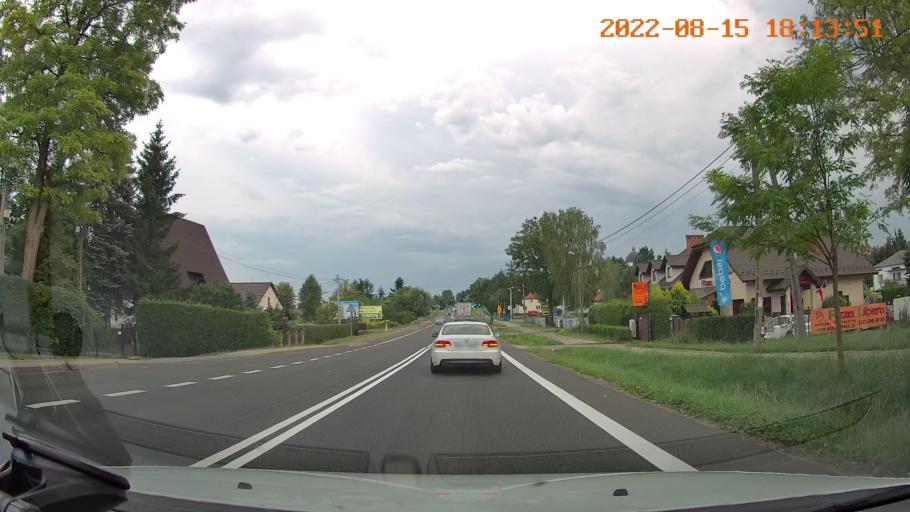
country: PL
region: Lesser Poland Voivodeship
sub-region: Powiat krakowski
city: Michalowice
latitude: 50.1615
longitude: 19.9796
